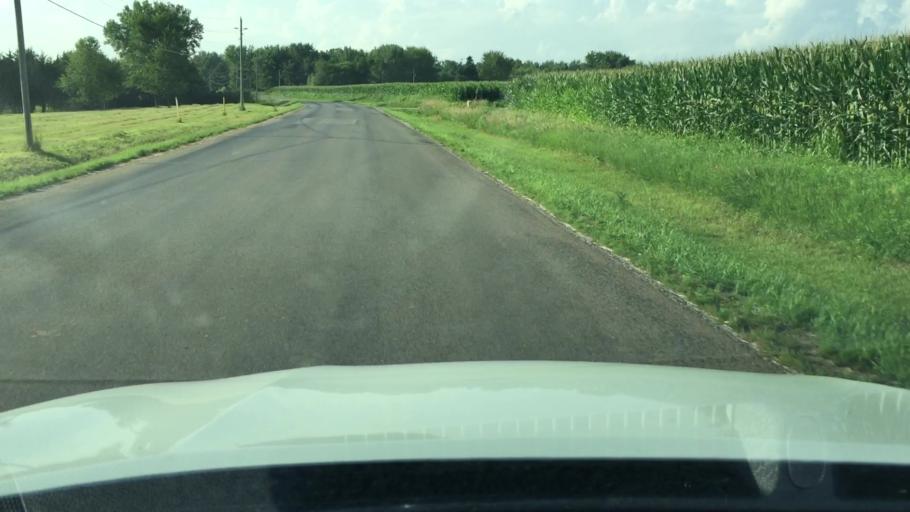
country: US
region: Iowa
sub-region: Johnson County
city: North Liberty
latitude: 41.8121
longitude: -91.6149
